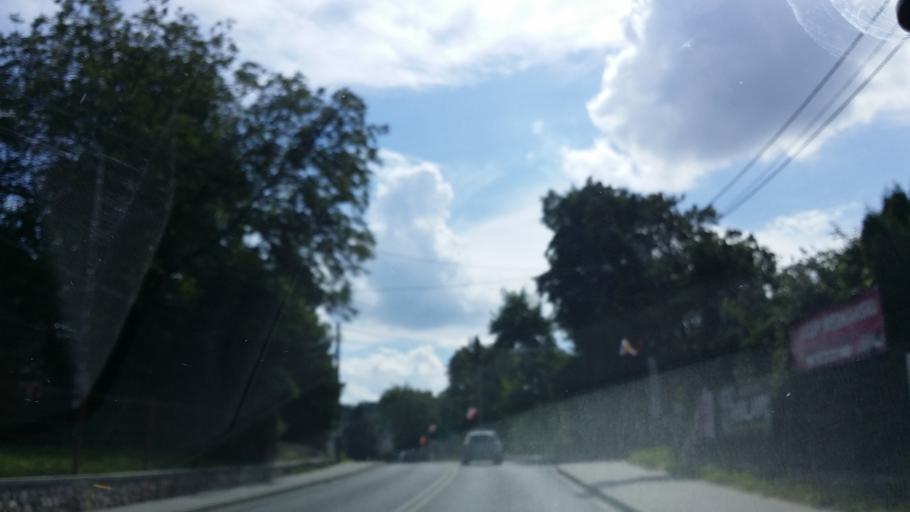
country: PL
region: Lesser Poland Voivodeship
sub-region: Powiat wielicki
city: Wieliczka
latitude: 49.9837
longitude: 20.0704
